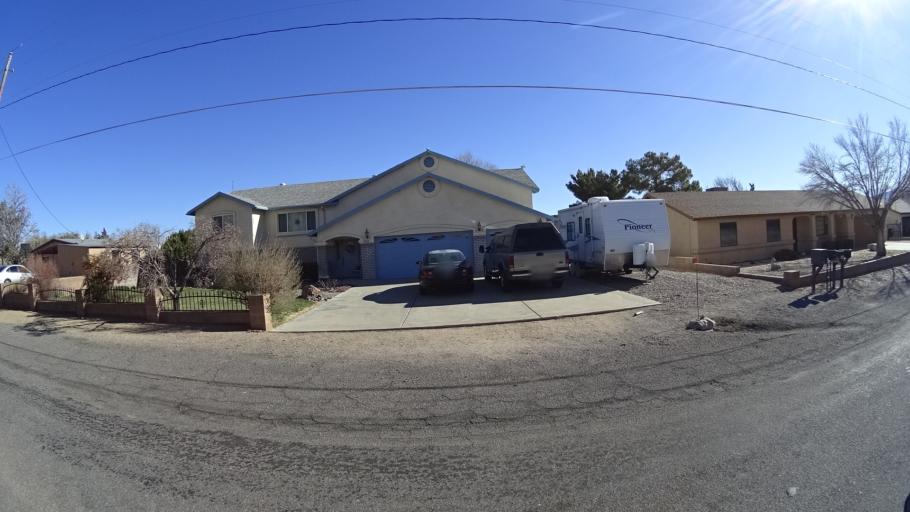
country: US
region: Arizona
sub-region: Mohave County
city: New Kingman-Butler
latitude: 35.2658
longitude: -114.0453
